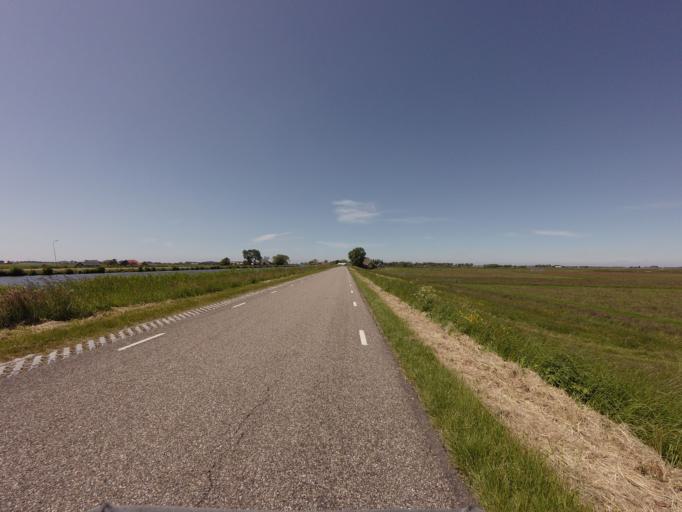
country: NL
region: North Holland
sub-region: Gemeente Zaanstad
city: Zaanstad
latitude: 52.5423
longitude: 4.8272
